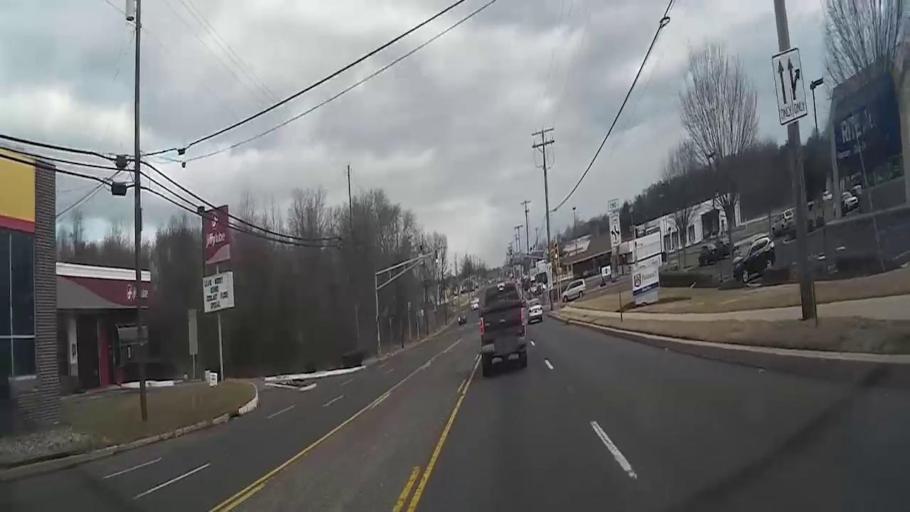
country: US
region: New Jersey
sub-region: Camden County
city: Stratford
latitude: 39.8037
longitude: -75.0335
